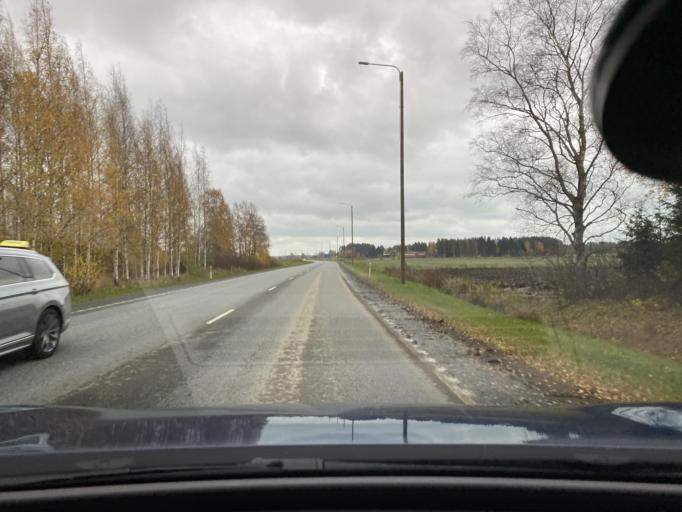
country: FI
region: Satakunta
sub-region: Rauma
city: Eura
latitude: 61.1612
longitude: 22.0871
